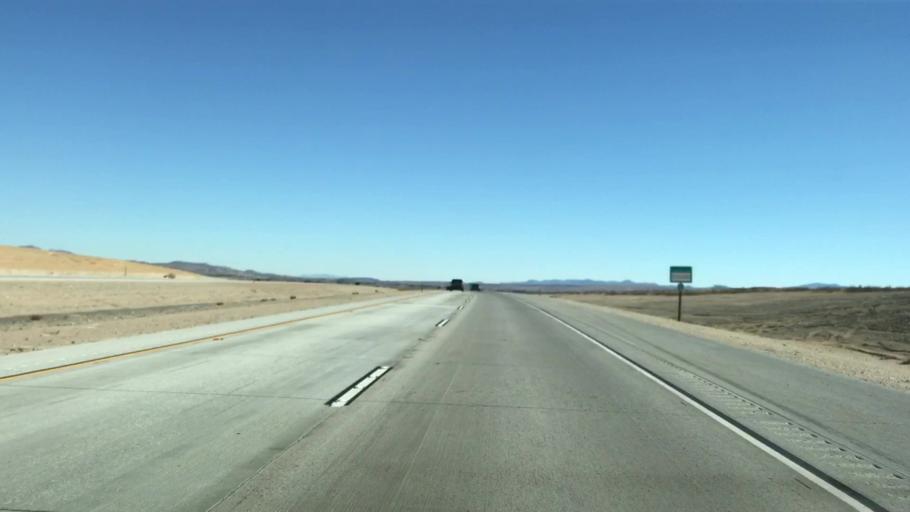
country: US
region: California
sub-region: San Bernardino County
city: Lenwood
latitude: 34.9144
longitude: -117.2345
